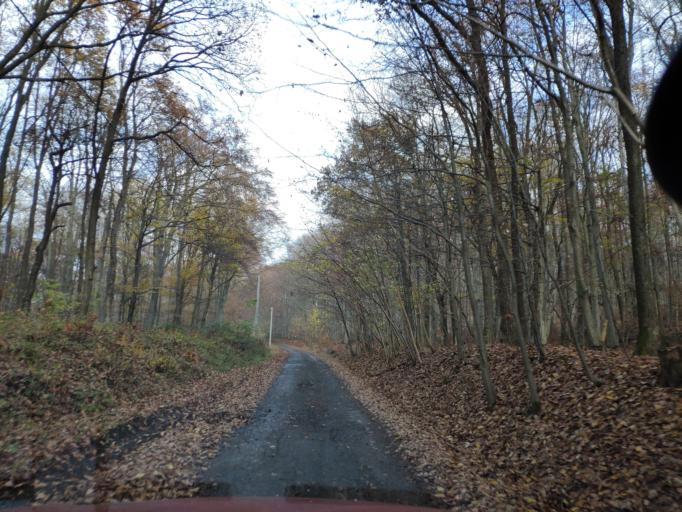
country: SK
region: Kosicky
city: Secovce
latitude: 48.5821
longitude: 21.4849
